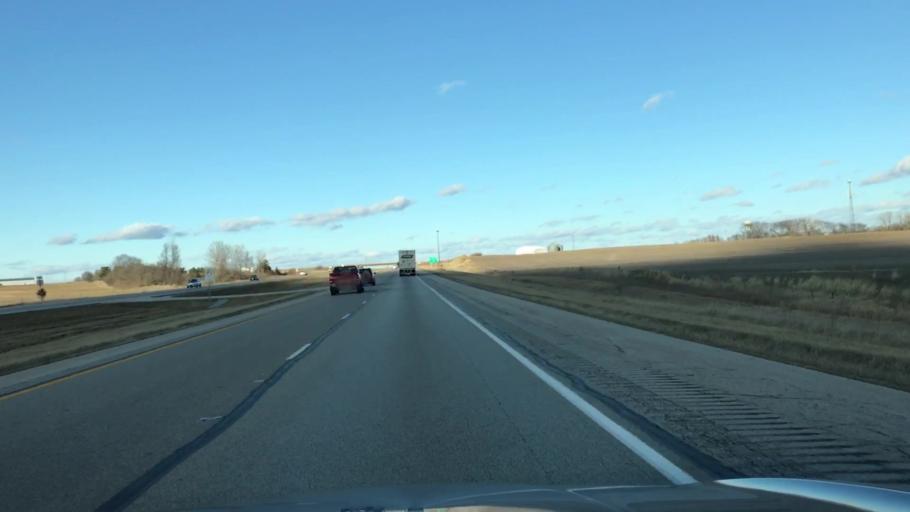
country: US
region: Illinois
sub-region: McLean County
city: Lexington
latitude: 40.6369
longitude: -88.8131
